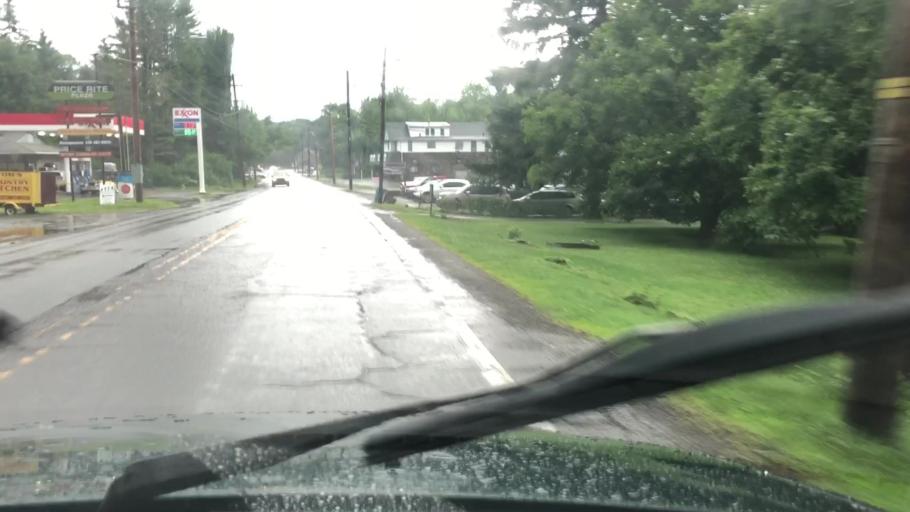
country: US
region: Pennsylvania
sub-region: Monroe County
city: Mountainhome
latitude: 41.1776
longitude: -75.2696
